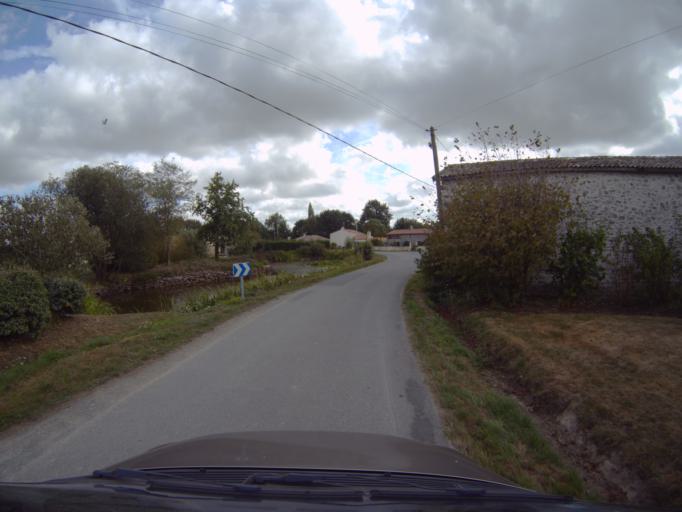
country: FR
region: Pays de la Loire
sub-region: Departement de la Loire-Atlantique
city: La Planche
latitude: 47.0256
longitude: -1.4102
